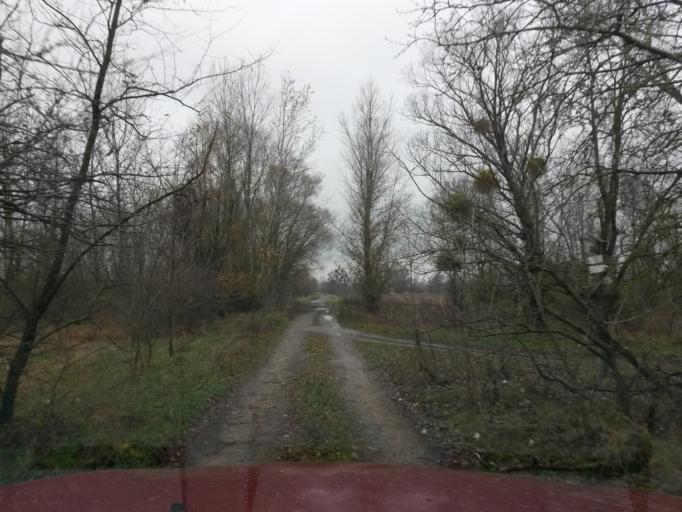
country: SK
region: Kosicky
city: Cierna nad Tisou
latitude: 48.5252
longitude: 21.9576
